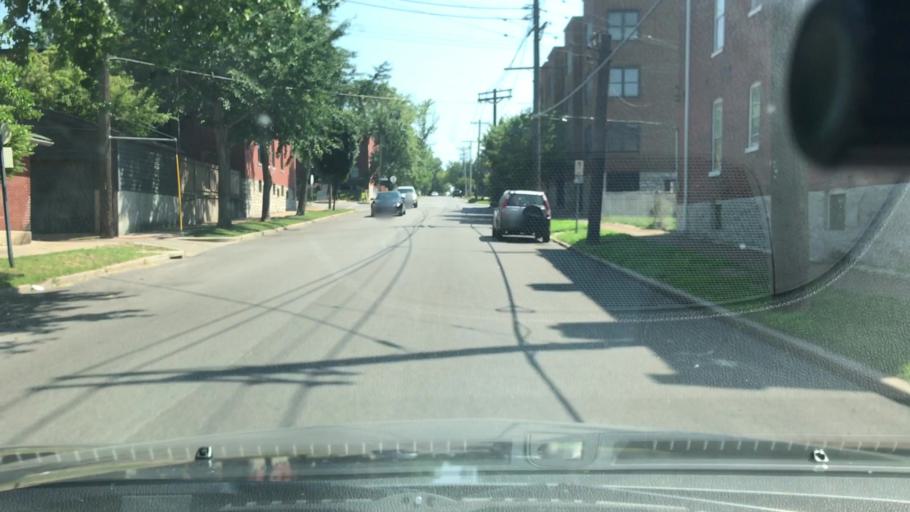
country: US
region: Missouri
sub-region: City of Saint Louis
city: St. Louis
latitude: 38.5987
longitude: -90.2503
